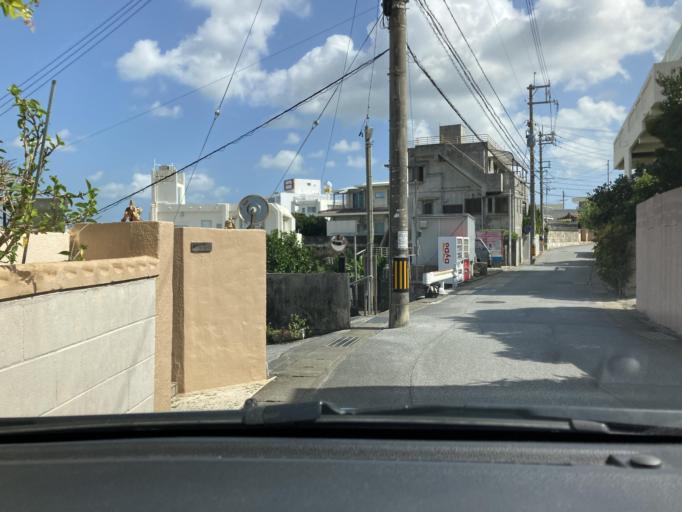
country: JP
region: Okinawa
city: Tomigusuku
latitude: 26.1971
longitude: 127.6752
